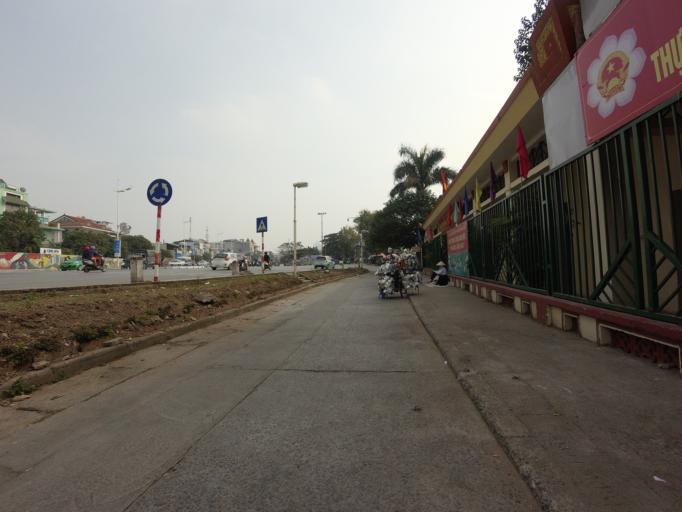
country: VN
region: Ha Noi
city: Tay Ho
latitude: 21.0594
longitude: 105.8339
